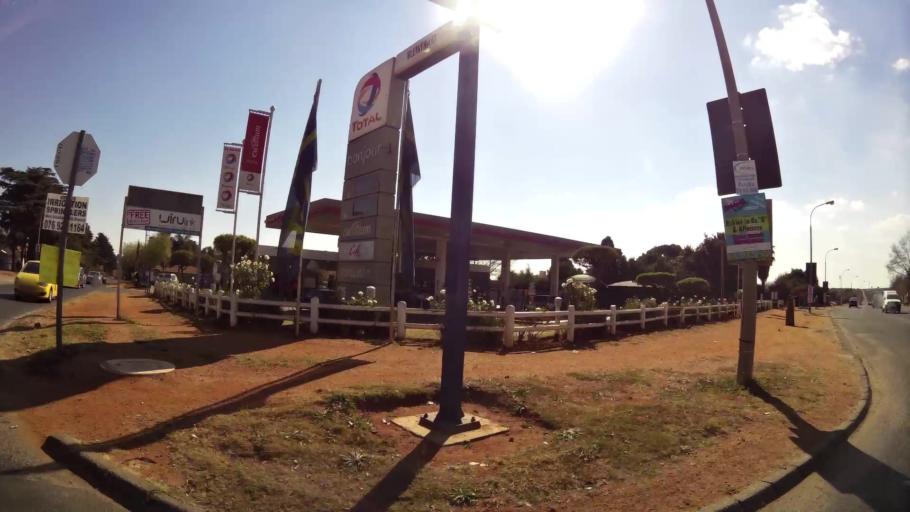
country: ZA
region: Gauteng
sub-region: Ekurhuleni Metropolitan Municipality
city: Tembisa
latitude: -26.0711
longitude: 28.2448
